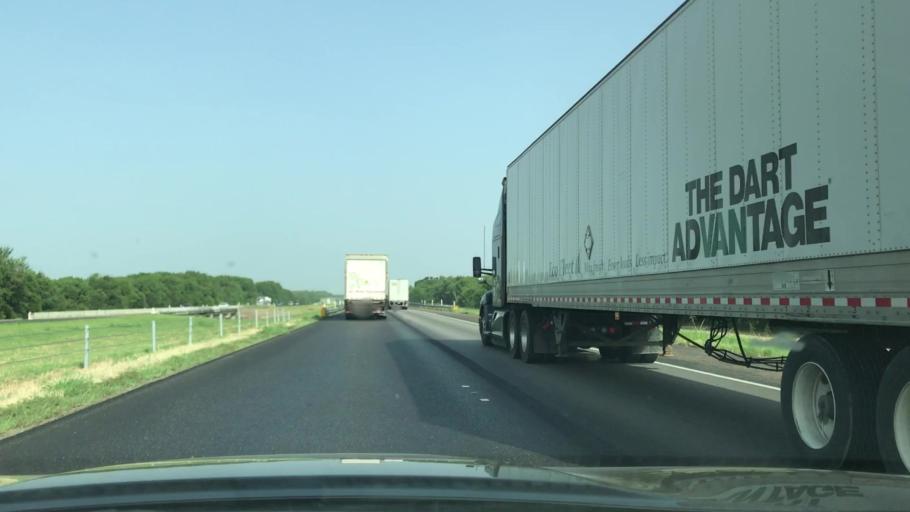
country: US
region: Texas
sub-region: Kaufman County
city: Terrell
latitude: 32.6731
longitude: -96.1629
